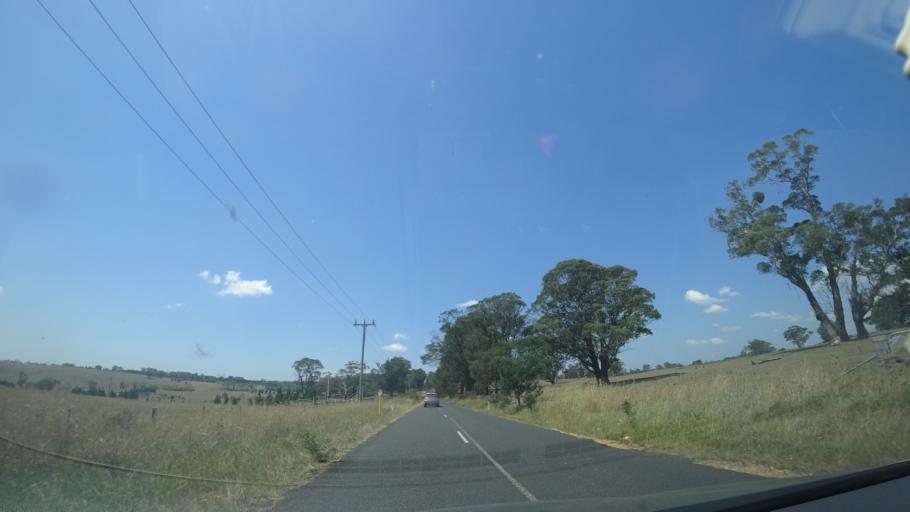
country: AU
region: New South Wales
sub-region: Wingecarribee
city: Bundanoon
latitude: -34.6102
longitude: 150.2683
